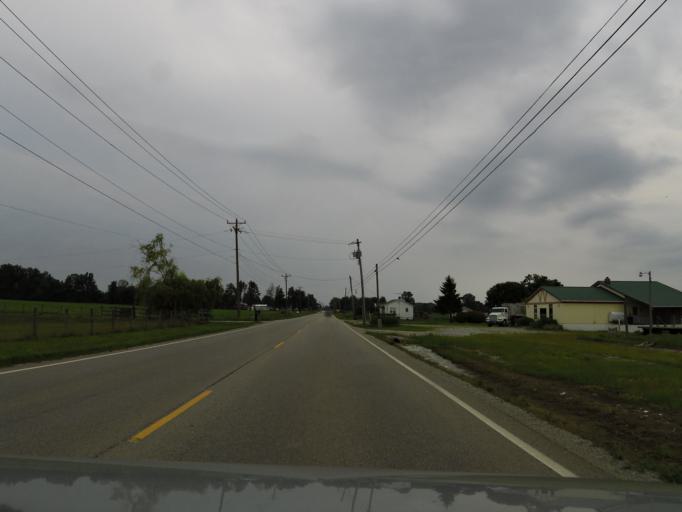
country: US
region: Ohio
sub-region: Brown County
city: Georgetown
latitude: 38.9205
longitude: -83.9033
